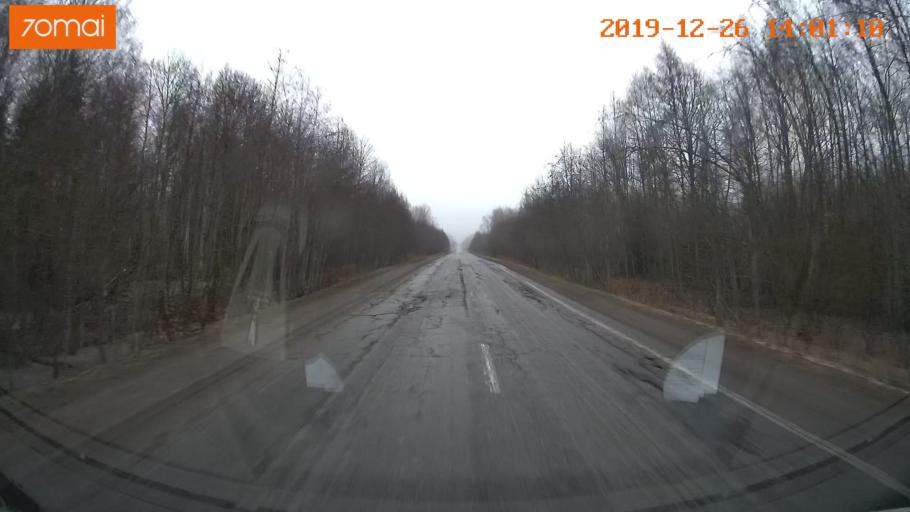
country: RU
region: Jaroslavl
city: Poshekhon'ye
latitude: 58.5525
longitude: 38.7585
